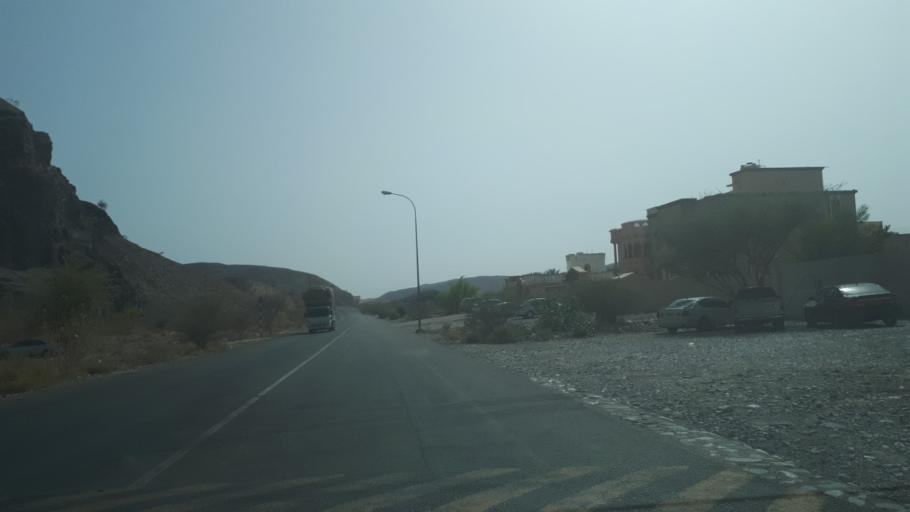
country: OM
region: Muhafazat ad Dakhiliyah
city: Bahla'
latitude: 23.2061
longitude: 56.9552
